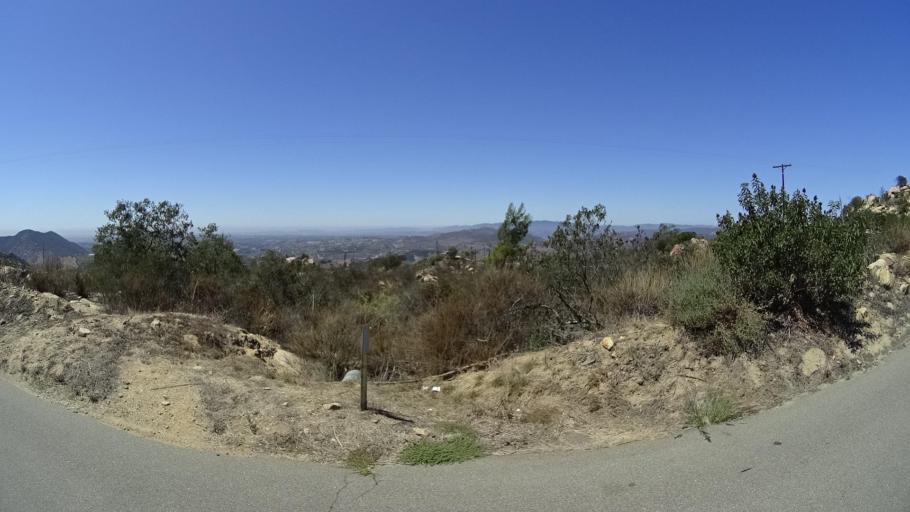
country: US
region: California
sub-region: San Diego County
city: Rainbow
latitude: 33.3960
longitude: -117.1300
